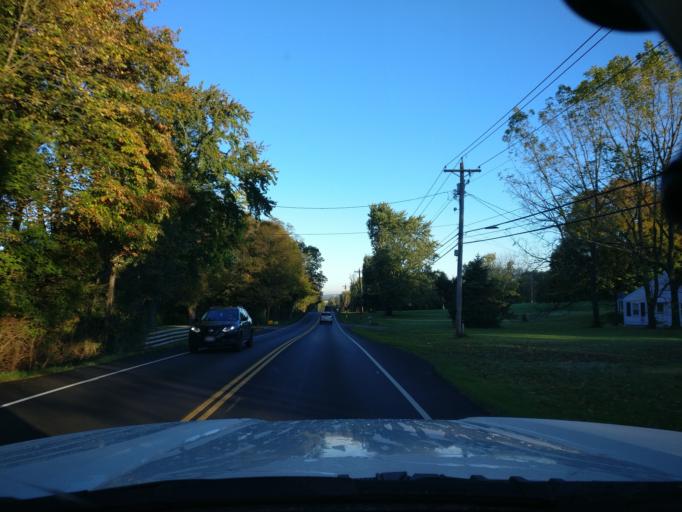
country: US
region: Ohio
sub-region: Warren County
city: Hunter
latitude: 39.5240
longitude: -84.2778
